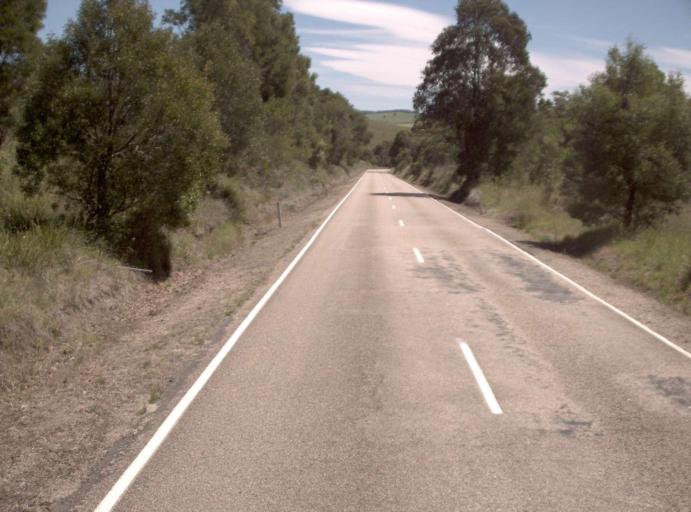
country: AU
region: Victoria
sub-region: East Gippsland
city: Lakes Entrance
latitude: -37.2550
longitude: 148.2486
